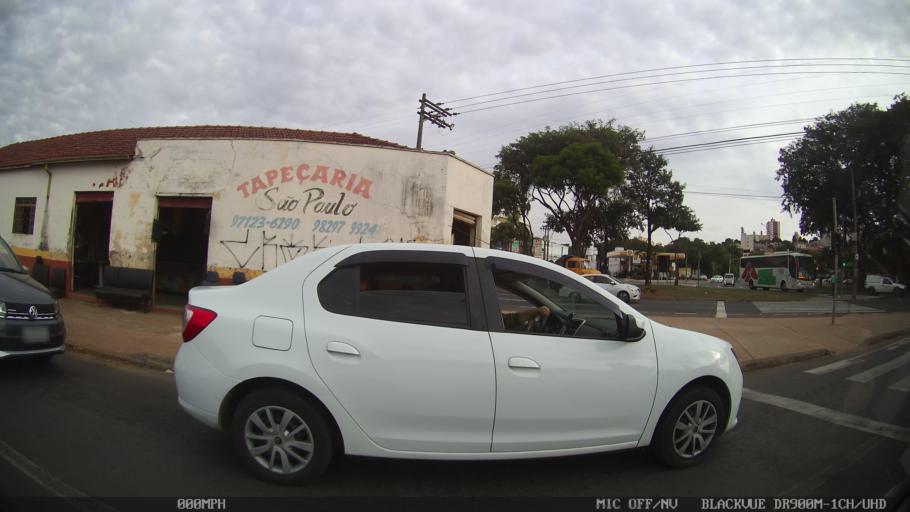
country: BR
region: Sao Paulo
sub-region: Piracicaba
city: Piracicaba
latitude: -22.7385
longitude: -47.6296
